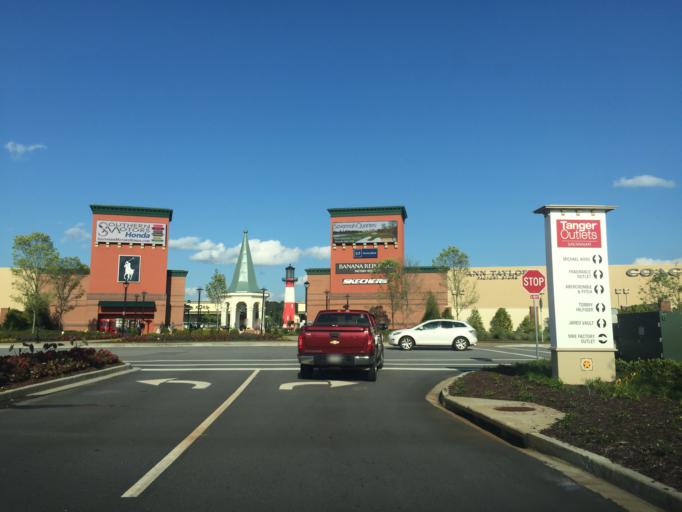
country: US
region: Georgia
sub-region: Chatham County
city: Pooler
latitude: 32.1348
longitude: -81.2448
